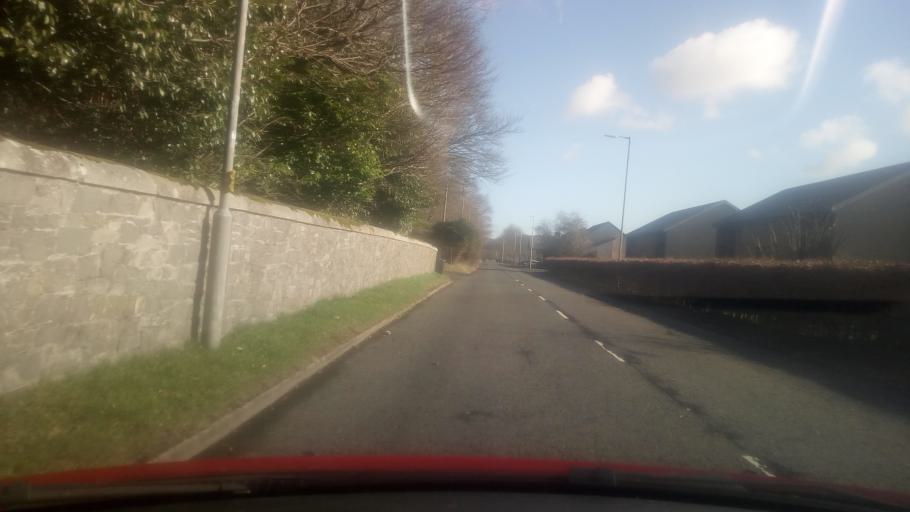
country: GB
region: Scotland
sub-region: The Scottish Borders
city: Selkirk
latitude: 55.5516
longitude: -2.8564
